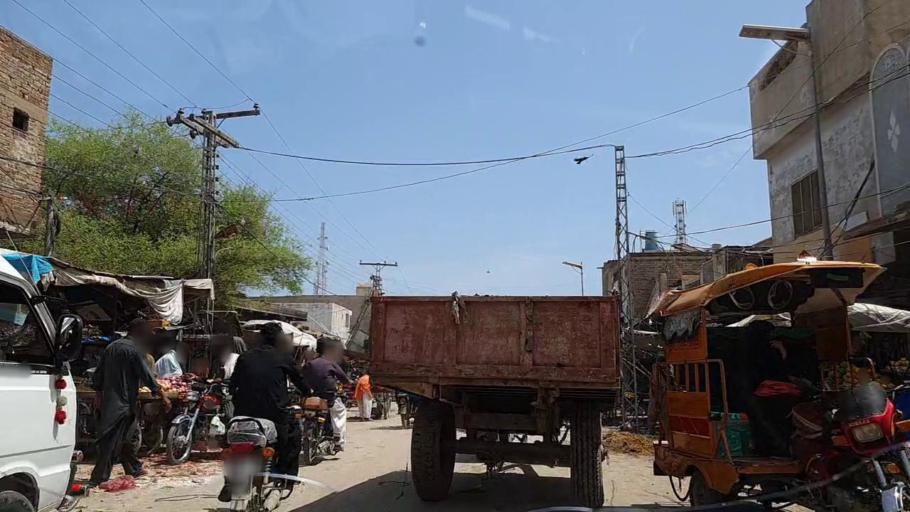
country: PK
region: Sindh
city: Naushahro Firoz
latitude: 26.8417
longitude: 68.1189
